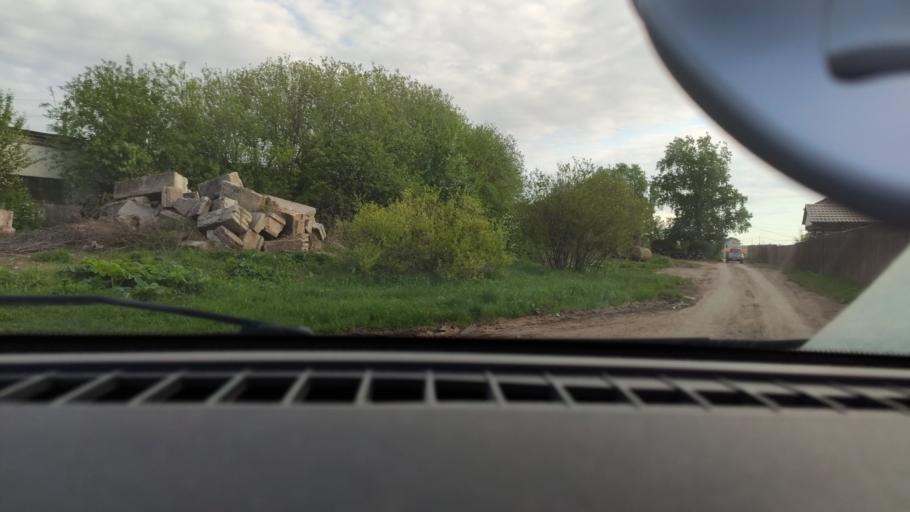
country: RU
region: Perm
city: Ferma
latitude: 57.9421
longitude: 56.3599
